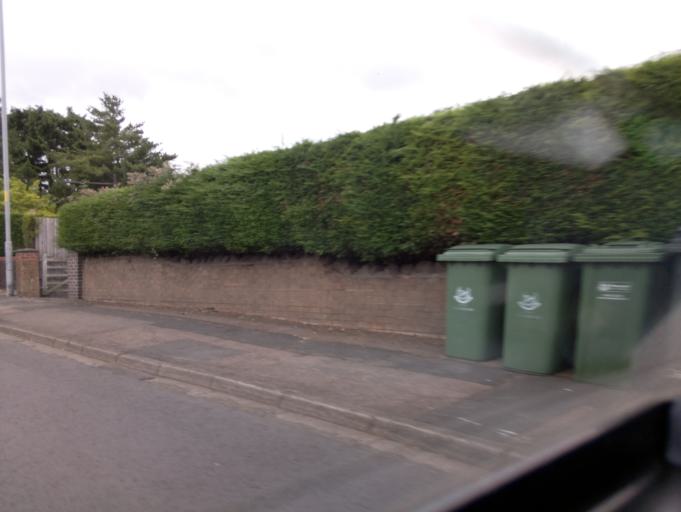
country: GB
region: England
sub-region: Worcestershire
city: Worcester
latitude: 52.1753
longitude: -2.2131
